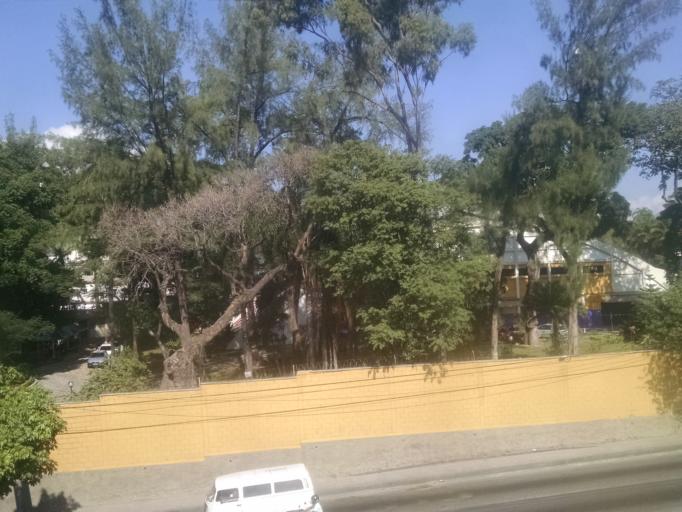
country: BR
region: Rio de Janeiro
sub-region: Duque De Caxias
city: Duque de Caxias
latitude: -22.8507
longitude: -43.3184
